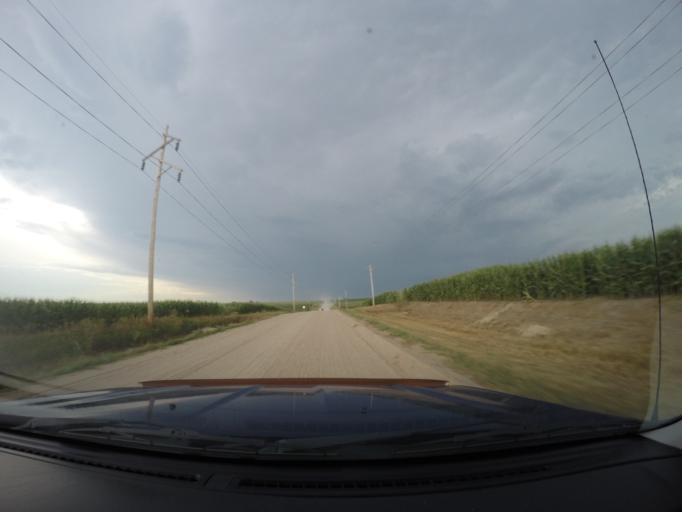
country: US
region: Nebraska
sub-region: Buffalo County
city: Kearney
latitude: 40.8441
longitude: -99.2179
